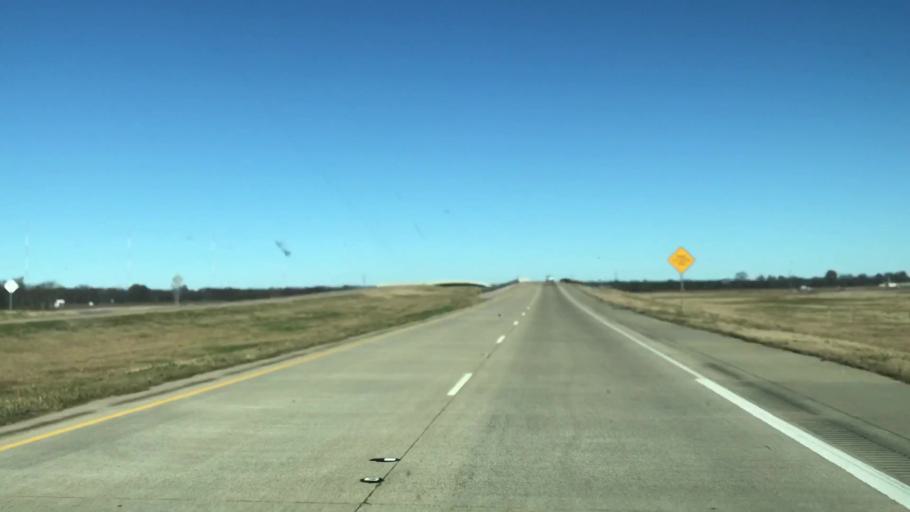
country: US
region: Louisiana
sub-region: Caddo Parish
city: Blanchard
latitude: 32.6722
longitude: -93.8489
